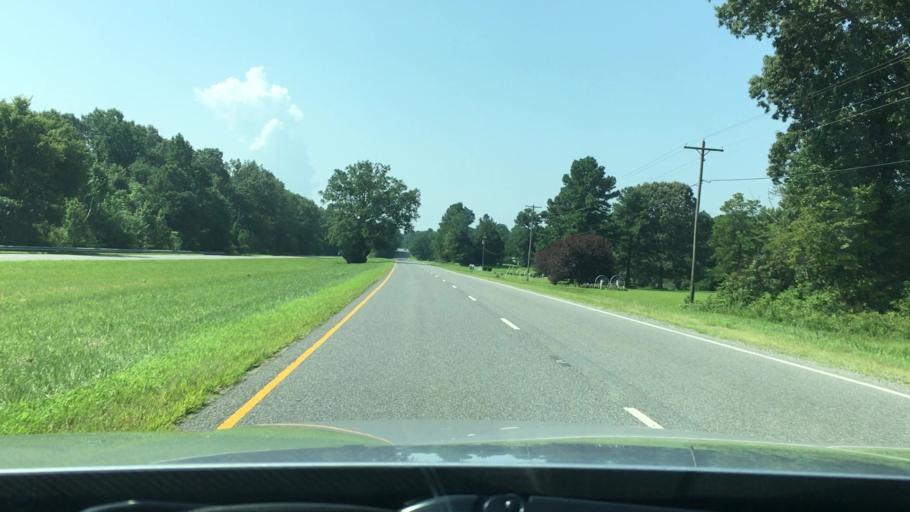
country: US
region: Virginia
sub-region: Caroline County
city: Bowling Green
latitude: 38.0105
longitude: -77.4131
